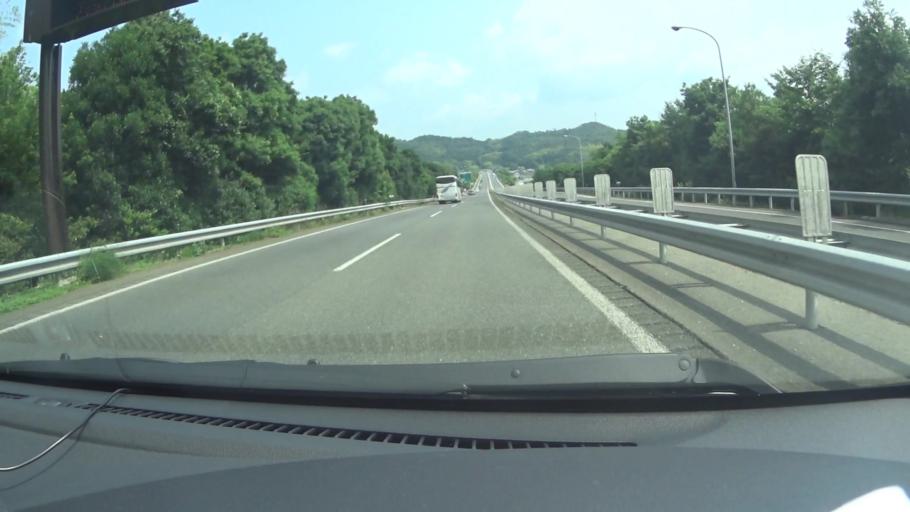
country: JP
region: Kyoto
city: Kameoka
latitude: 35.0460
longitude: 135.5348
